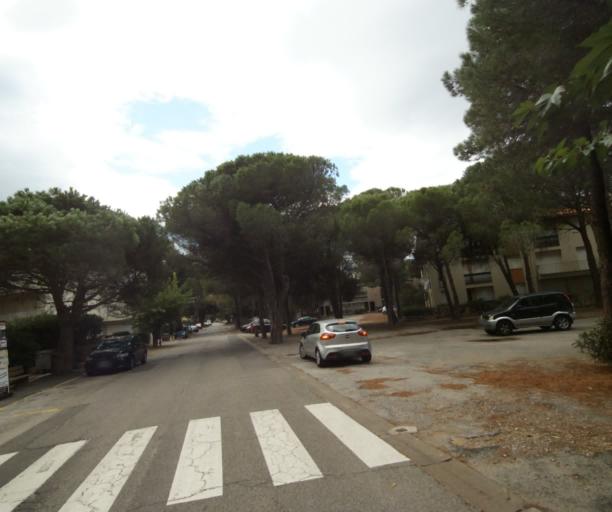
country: FR
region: Languedoc-Roussillon
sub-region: Departement des Pyrenees-Orientales
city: Argelers
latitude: 42.5633
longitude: 3.0450
